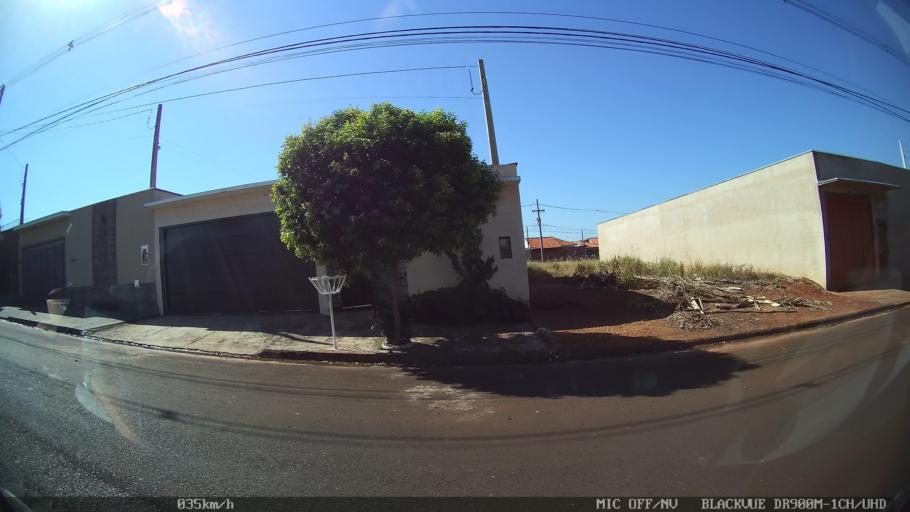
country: BR
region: Sao Paulo
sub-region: Batatais
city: Batatais
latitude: -20.8877
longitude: -47.5655
